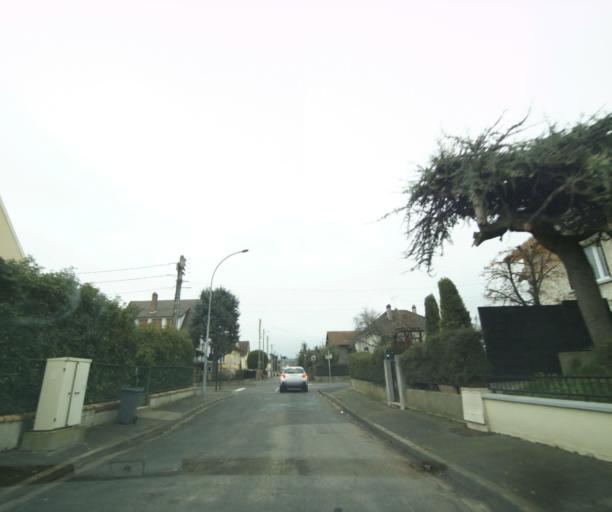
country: FR
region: Ile-de-France
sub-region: Departement du Val-de-Marne
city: Ablon-sur-Seine
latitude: 48.7269
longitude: 2.4282
